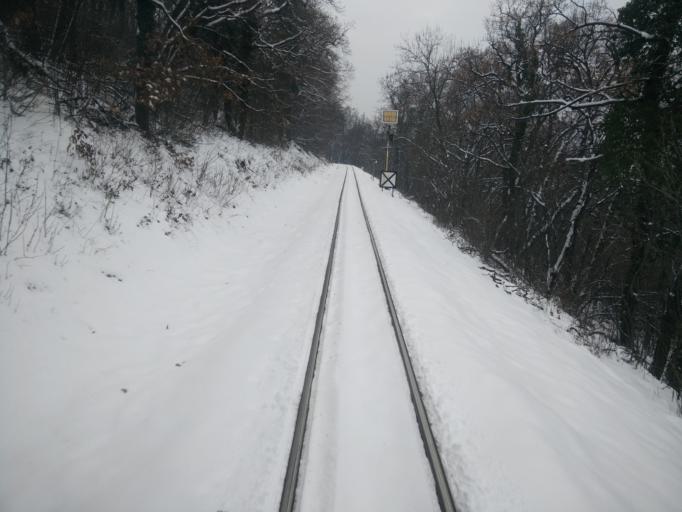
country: HU
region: Pest
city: Budakeszi
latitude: 47.5317
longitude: 18.9675
